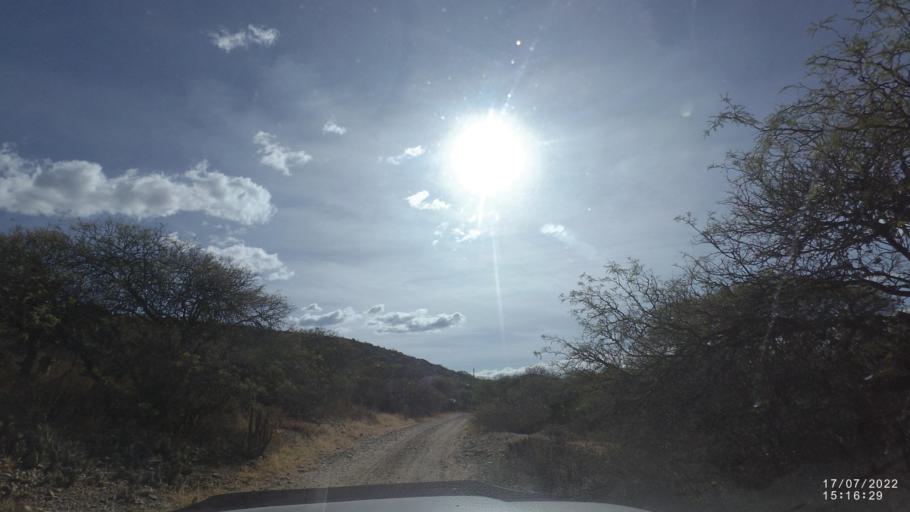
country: BO
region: Cochabamba
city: Capinota
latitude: -17.5540
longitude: -66.2646
